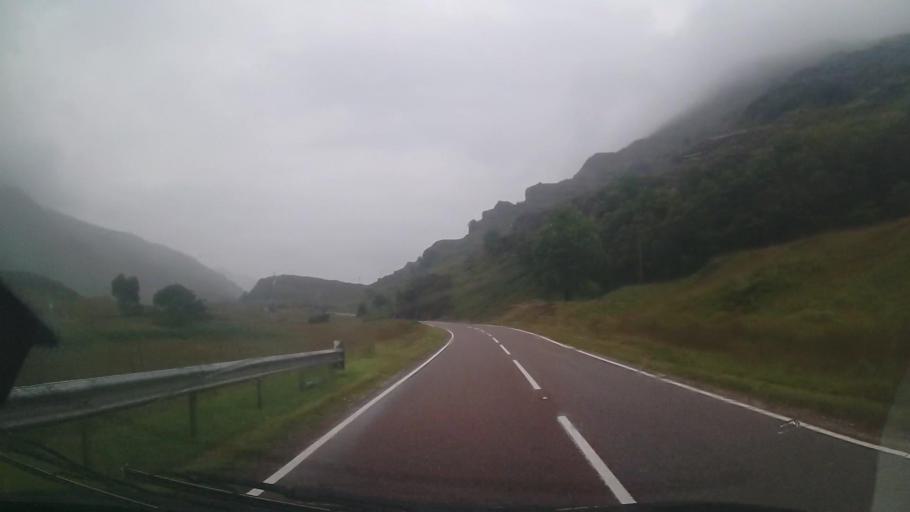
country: GB
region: Scotland
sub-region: Highland
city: Fort William
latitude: 56.8755
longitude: -5.5043
